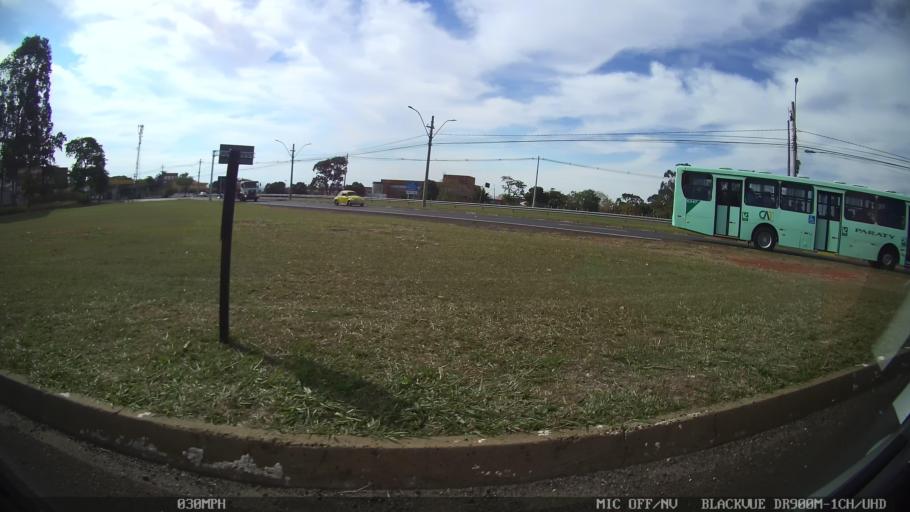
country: BR
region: Sao Paulo
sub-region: Araraquara
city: Araraquara
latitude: -21.8121
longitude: -48.1588
